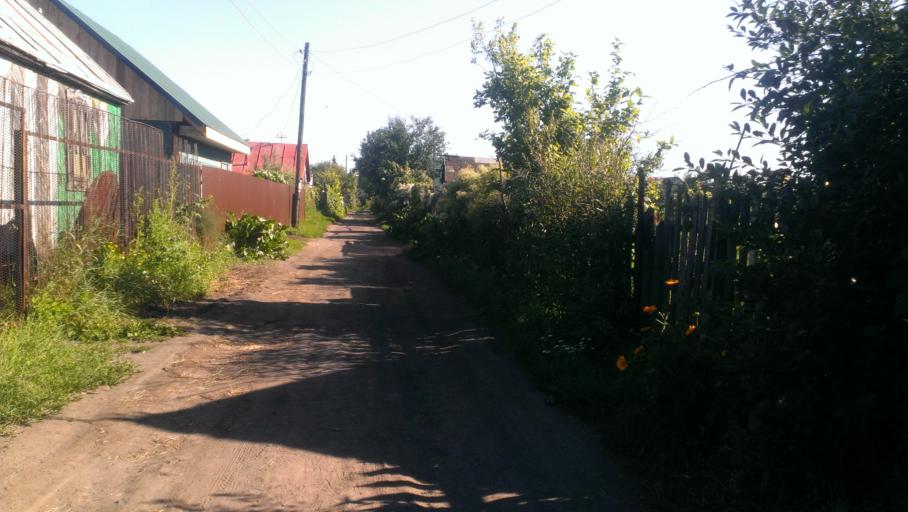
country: RU
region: Altai Krai
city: Novosilikatnyy
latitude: 53.3231
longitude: 83.6694
